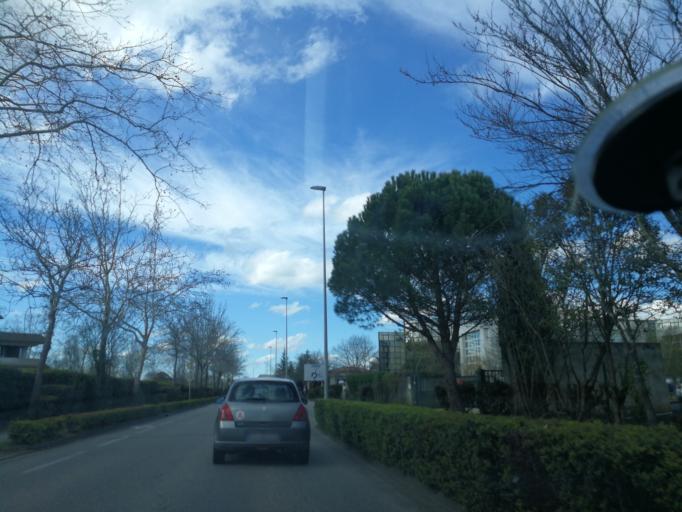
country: FR
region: Midi-Pyrenees
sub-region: Departement de la Haute-Garonne
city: Blagnac
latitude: 43.6351
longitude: 1.3763
